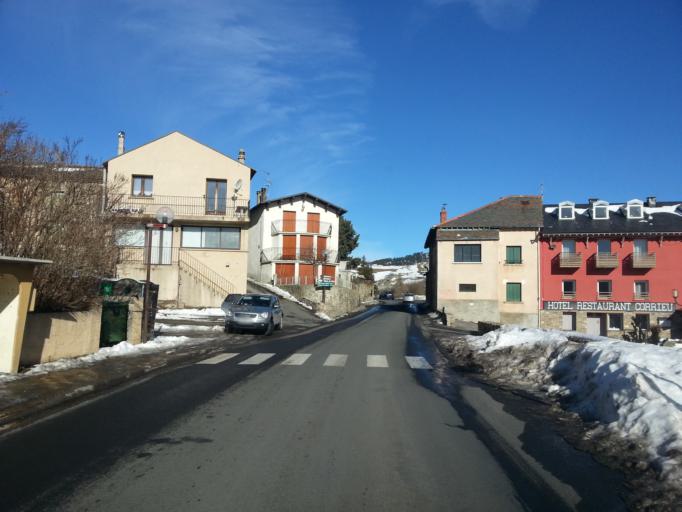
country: ES
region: Catalonia
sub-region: Provincia de Girona
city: Llivia
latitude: 42.5255
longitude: 2.1229
